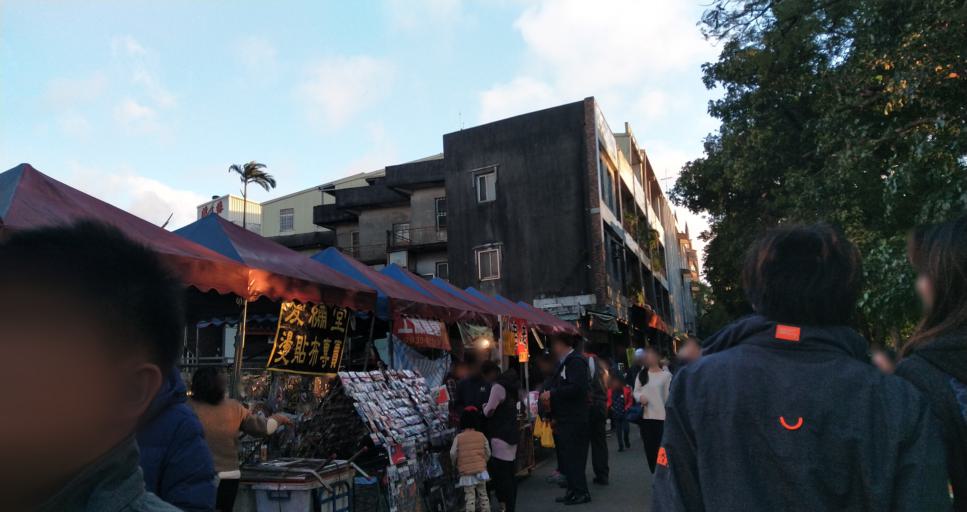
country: TW
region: Taiwan
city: Daxi
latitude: 24.8854
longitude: 121.2853
